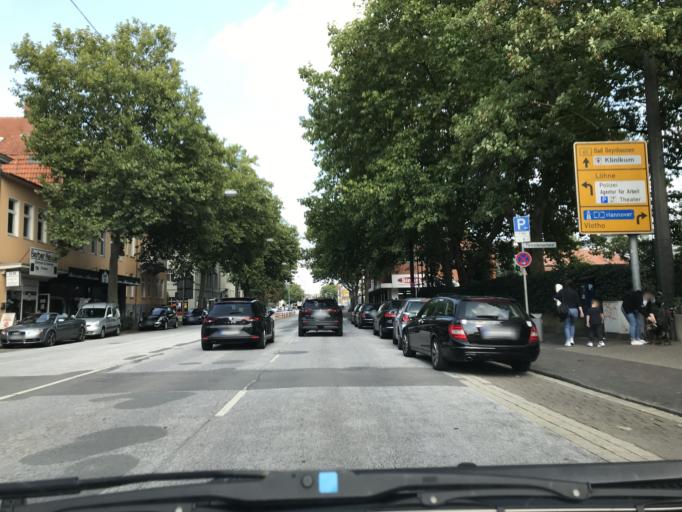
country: DE
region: North Rhine-Westphalia
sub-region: Regierungsbezirk Detmold
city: Herford
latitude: 52.1185
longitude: 8.6780
